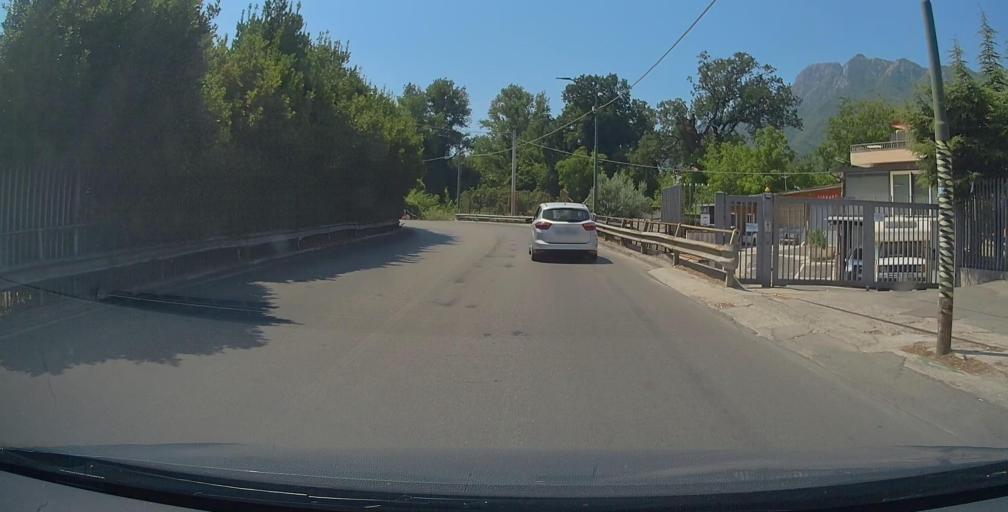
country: IT
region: Campania
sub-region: Provincia di Salerno
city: Cava De Tirreni
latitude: 40.7162
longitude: 14.6964
